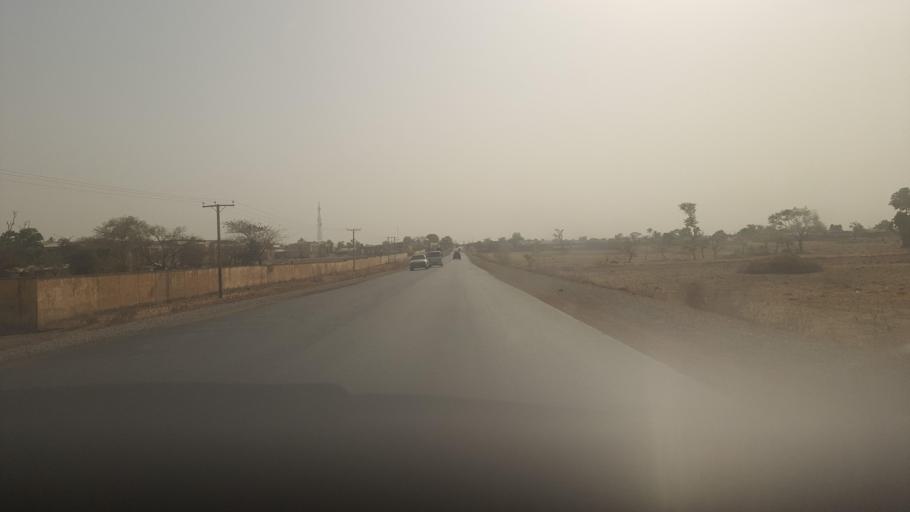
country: NG
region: Bauchi
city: Dindima
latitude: 10.2642
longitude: 10.0034
